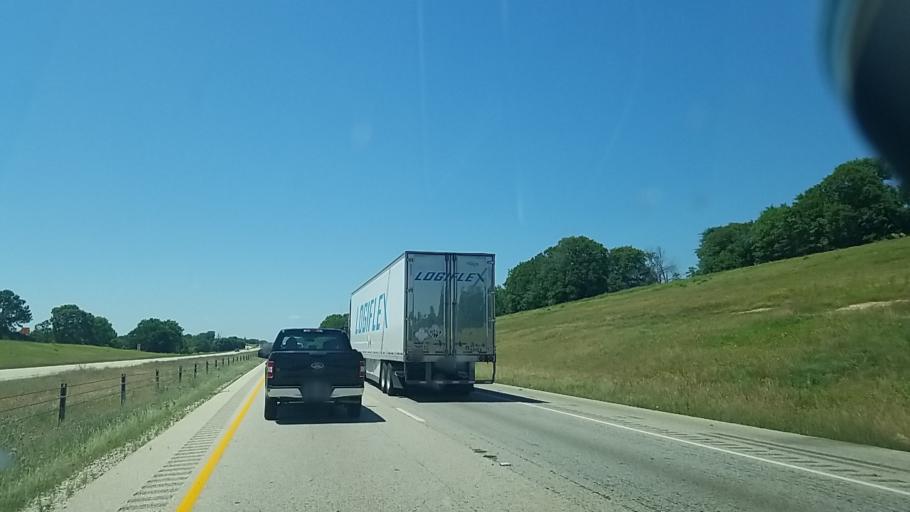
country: US
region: Texas
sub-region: Leon County
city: Buffalo
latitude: 31.4269
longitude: -96.0543
